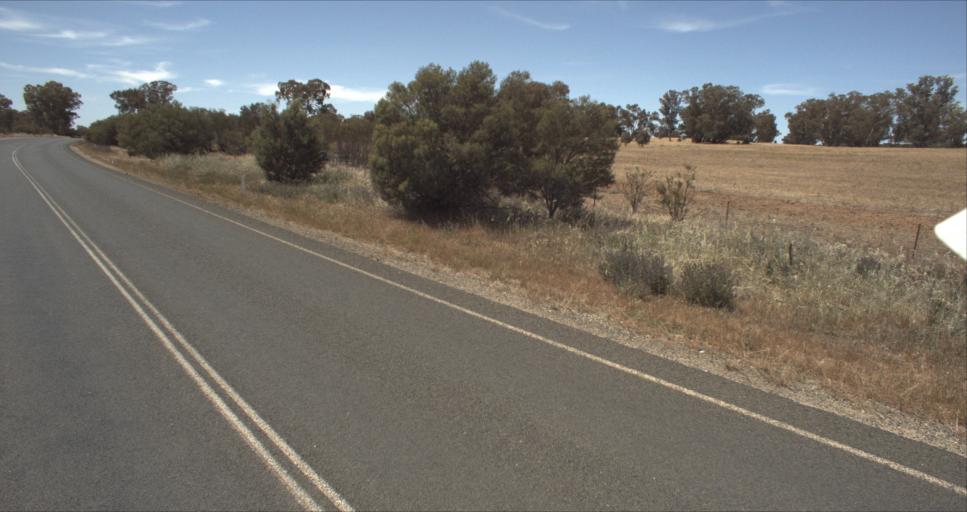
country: AU
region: New South Wales
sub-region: Leeton
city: Leeton
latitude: -34.6609
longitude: 146.4521
